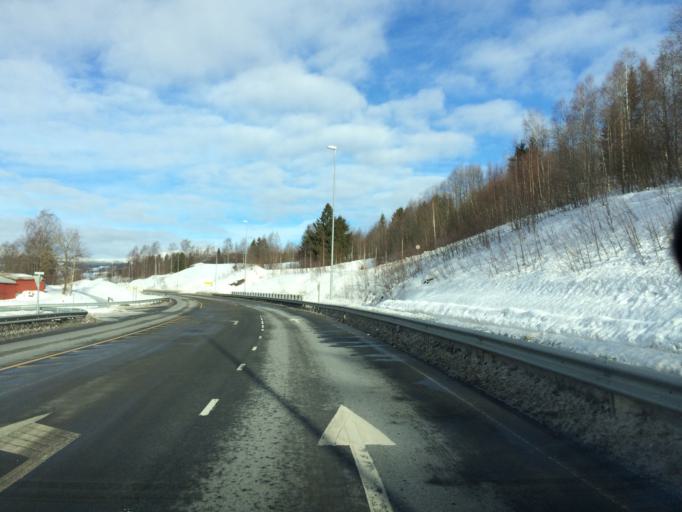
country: NO
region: Oppland
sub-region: Gausdal
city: Segalstad bru
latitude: 61.1898
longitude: 10.3177
